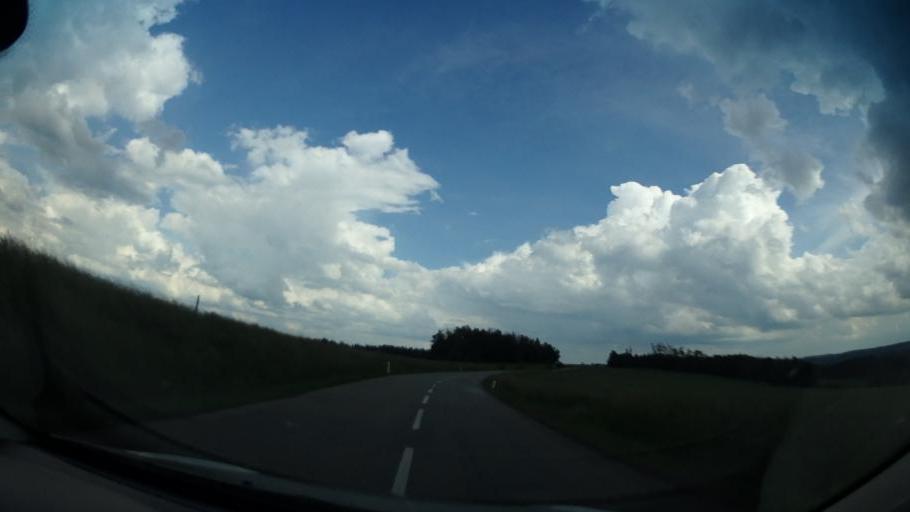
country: CZ
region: South Moravian
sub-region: Okres Brno-Venkov
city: Dolni Loucky
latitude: 49.3922
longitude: 16.3331
